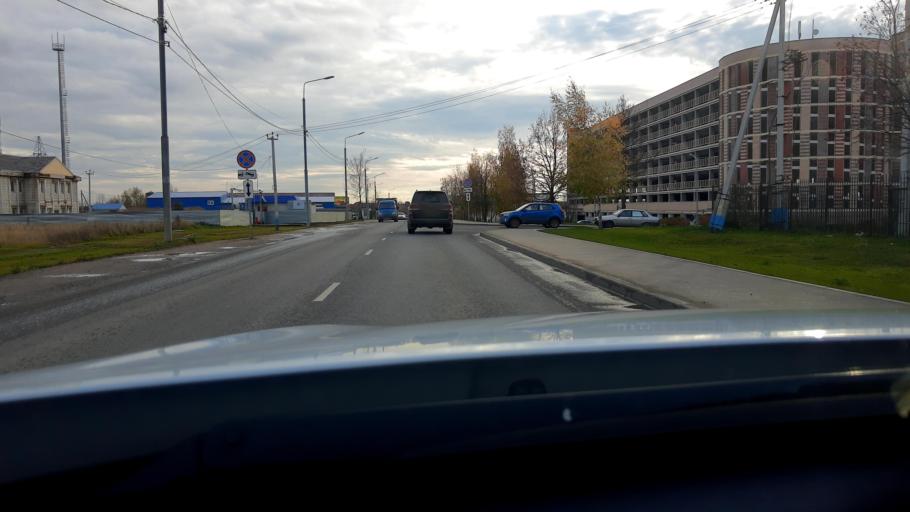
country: RU
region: Moskovskaya
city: Kokoshkino
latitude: 55.5435
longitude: 37.1550
